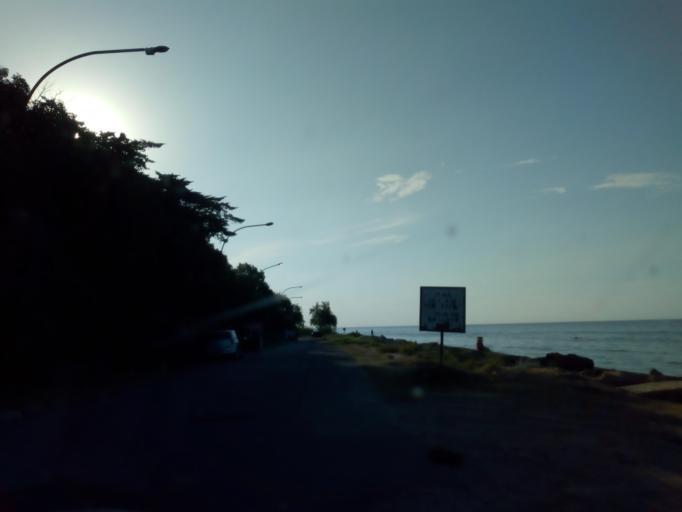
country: AR
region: Buenos Aires
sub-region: Partido de Ensenada
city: Ensenada
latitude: -34.7820
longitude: -58.0119
